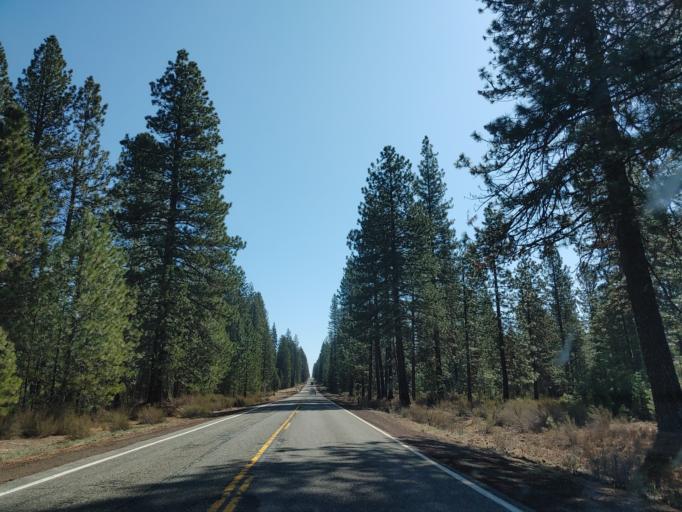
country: US
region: California
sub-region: Siskiyou County
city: McCloud
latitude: 41.2543
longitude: -122.0732
